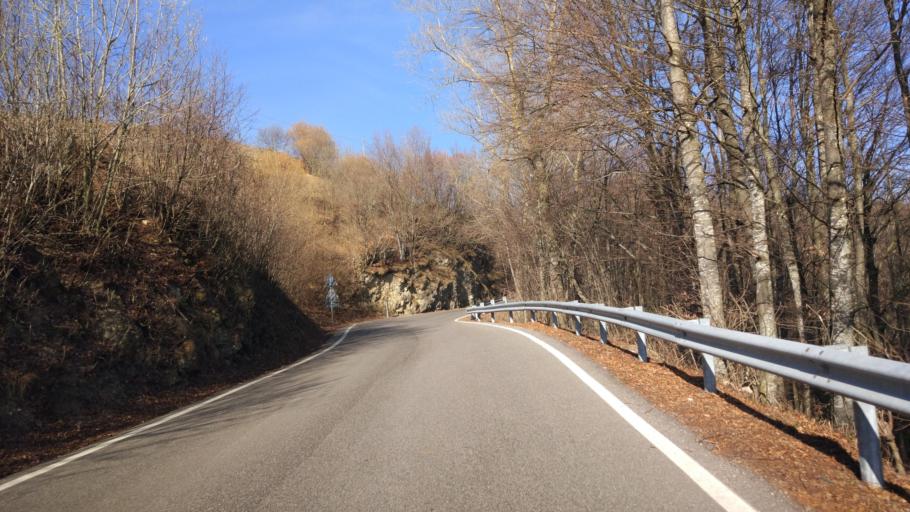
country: IT
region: Veneto
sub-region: Provincia di Verona
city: Selva di Progno
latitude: 45.6170
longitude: 11.1740
